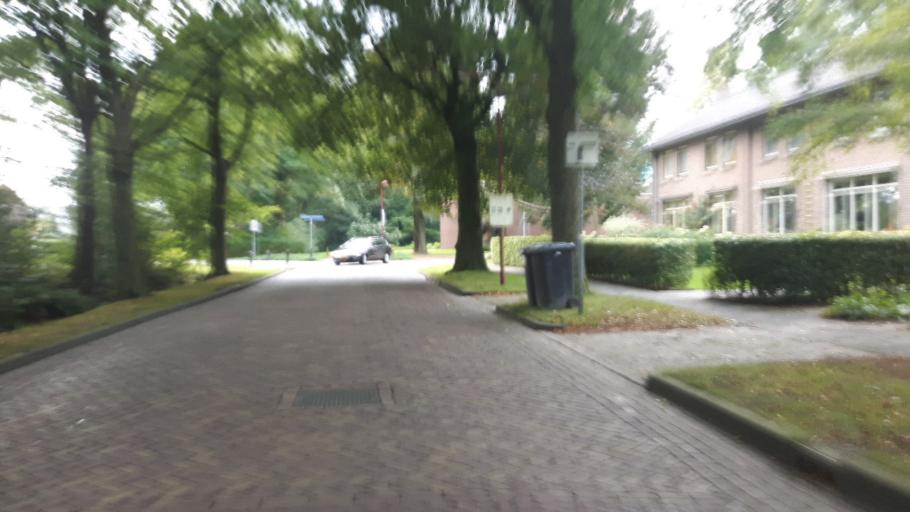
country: NL
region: Friesland
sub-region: Gemeente Heerenveen
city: Jubbega
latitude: 52.9891
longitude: 6.2863
